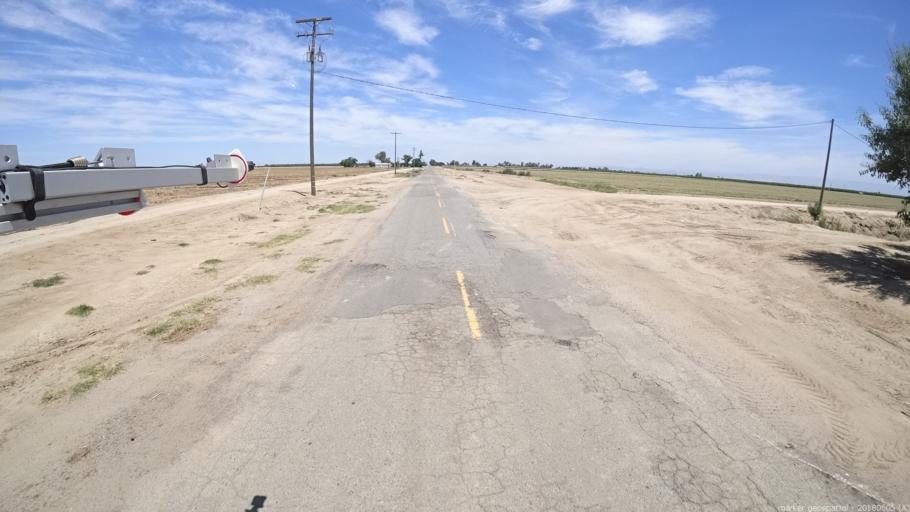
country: US
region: California
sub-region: Madera County
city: Chowchilla
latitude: 37.1017
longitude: -120.3652
